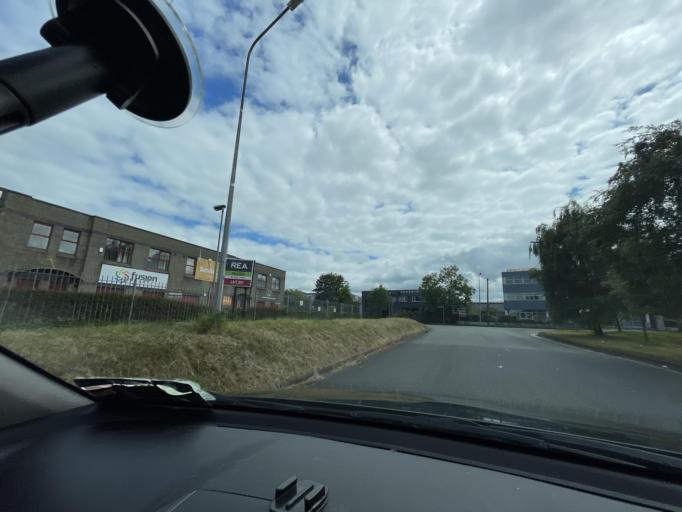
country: IE
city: Cherry Orchard
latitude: 53.3253
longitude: -6.3638
